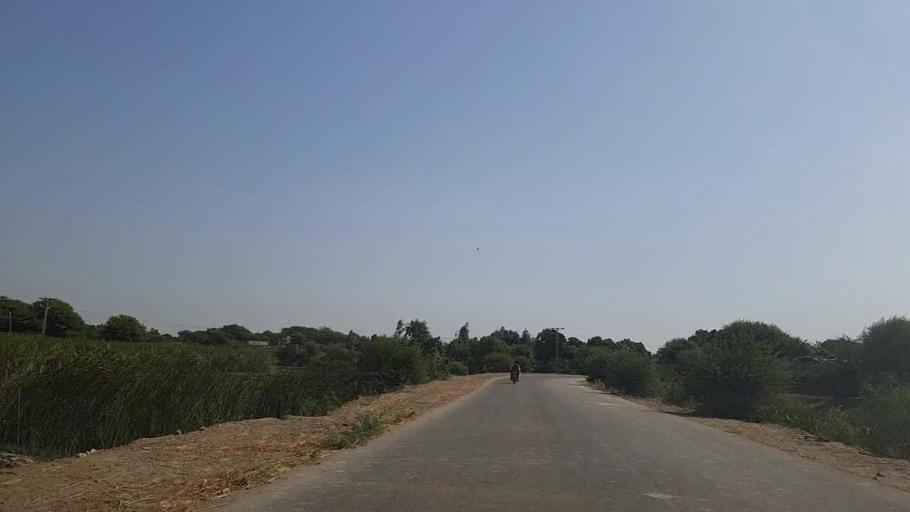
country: PK
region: Sindh
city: Daro Mehar
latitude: 24.7650
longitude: 68.2170
